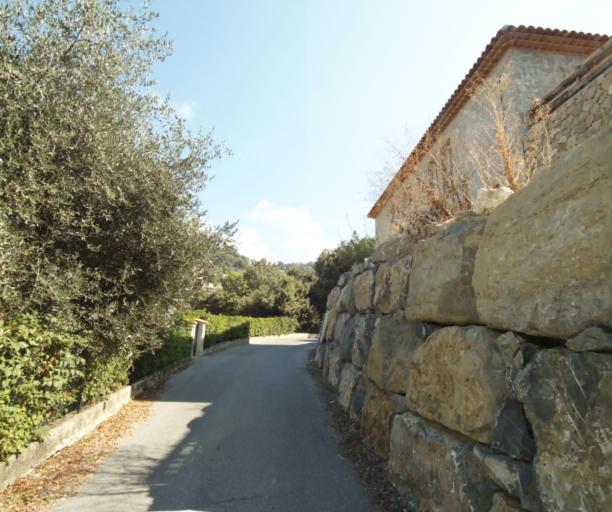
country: FR
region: Provence-Alpes-Cote d'Azur
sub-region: Departement des Alpes-Maritimes
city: Drap
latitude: 43.7518
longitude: 7.3243
